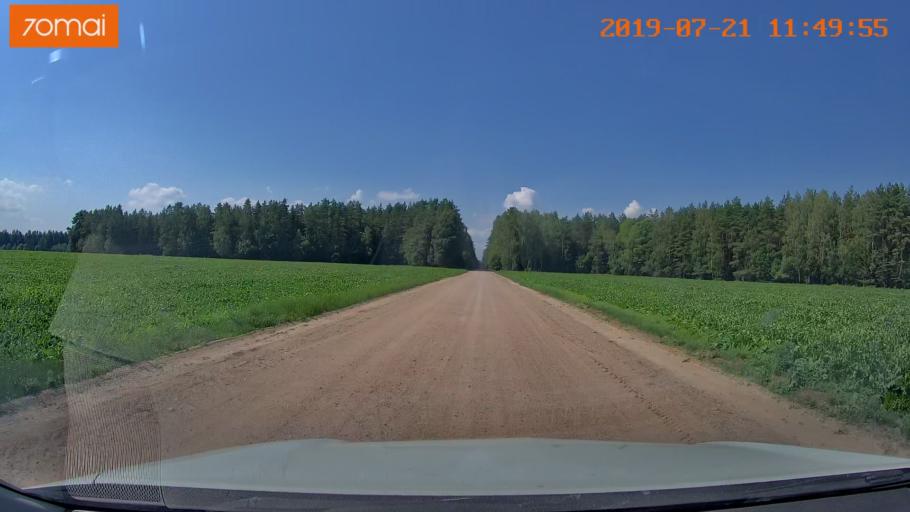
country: BY
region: Grodnenskaya
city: Lyubcha
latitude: 53.8899
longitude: 26.0331
